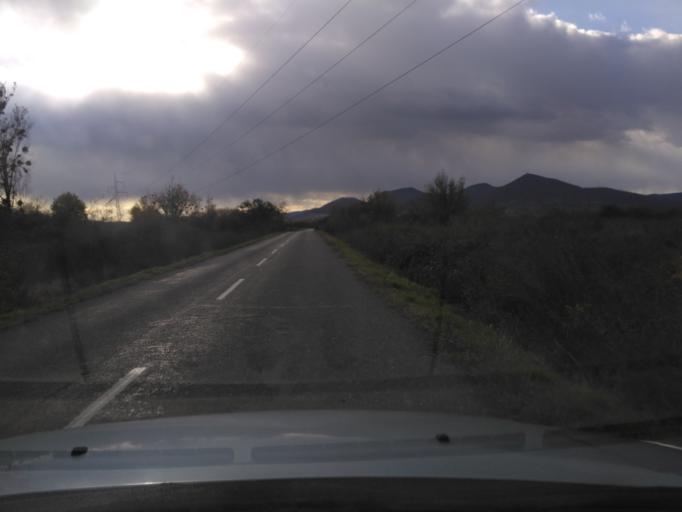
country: HU
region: Borsod-Abauj-Zemplen
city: Satoraljaujhely
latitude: 48.4135
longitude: 21.7171
